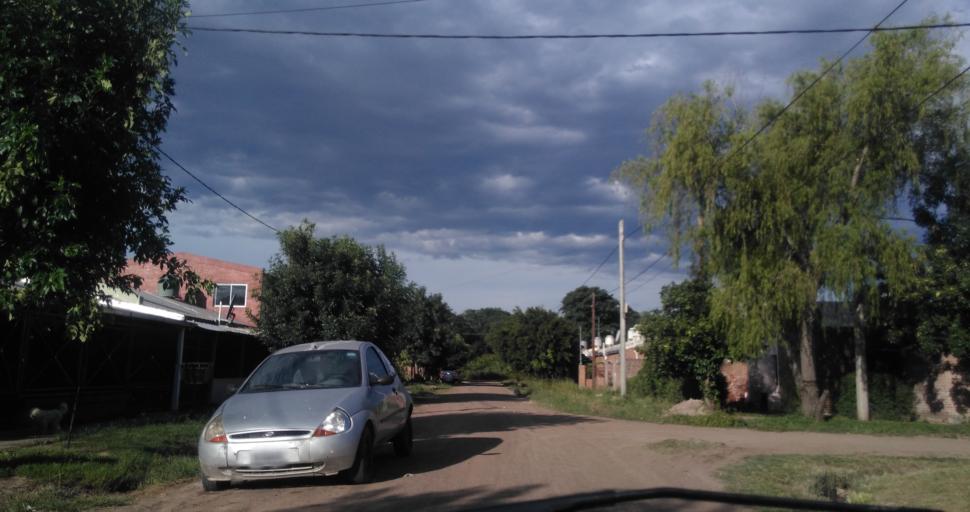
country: AR
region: Chaco
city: Fontana
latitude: -27.4101
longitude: -59.0275
